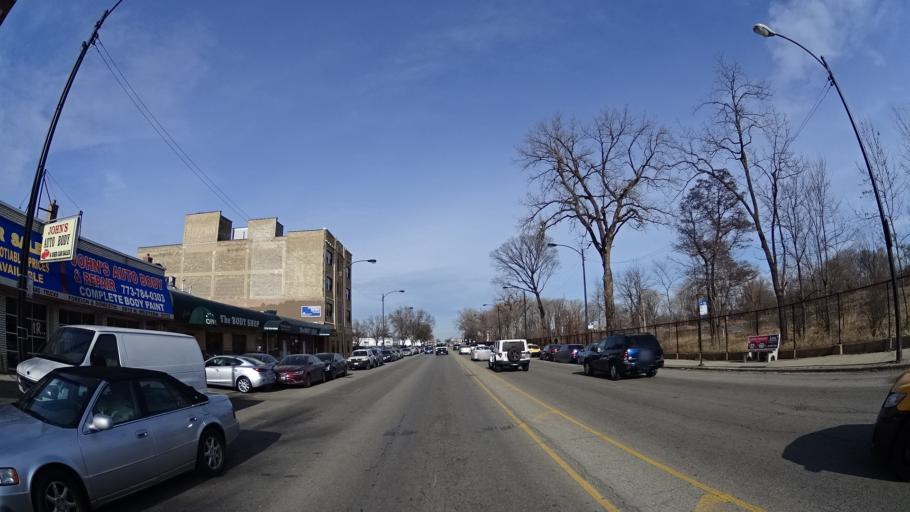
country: US
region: Illinois
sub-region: Cook County
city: Lincolnwood
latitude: 41.9871
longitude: -87.6896
